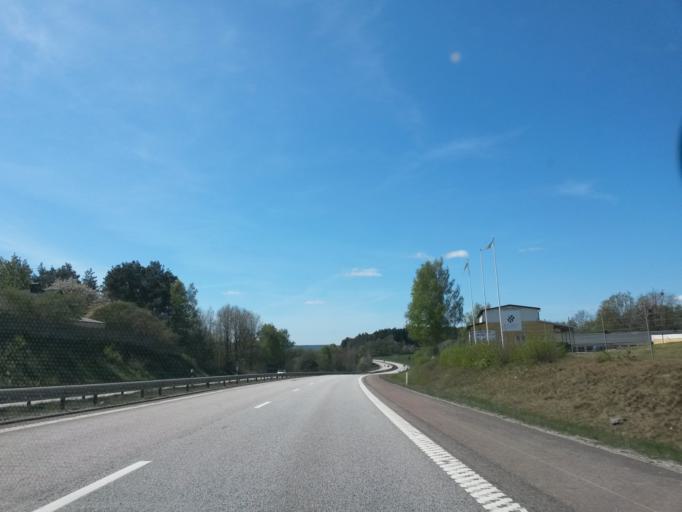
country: SE
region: Vaestra Goetaland
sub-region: Lerums Kommun
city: Stenkullen
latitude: 57.7938
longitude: 12.3481
